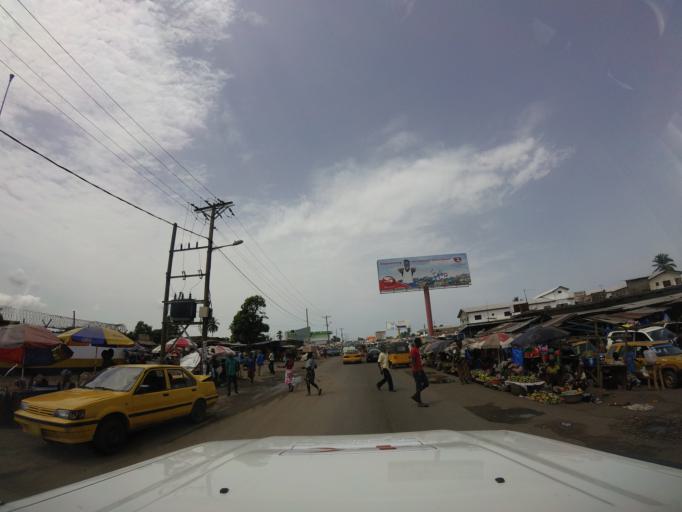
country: LR
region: Montserrado
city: Monrovia
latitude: 6.3766
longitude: -10.7849
